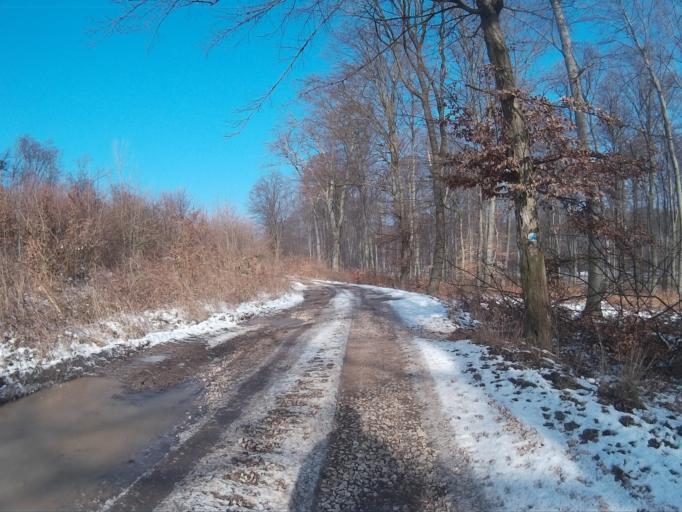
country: HU
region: Komarom-Esztergom
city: Labatlan
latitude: 47.6866
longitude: 18.5076
